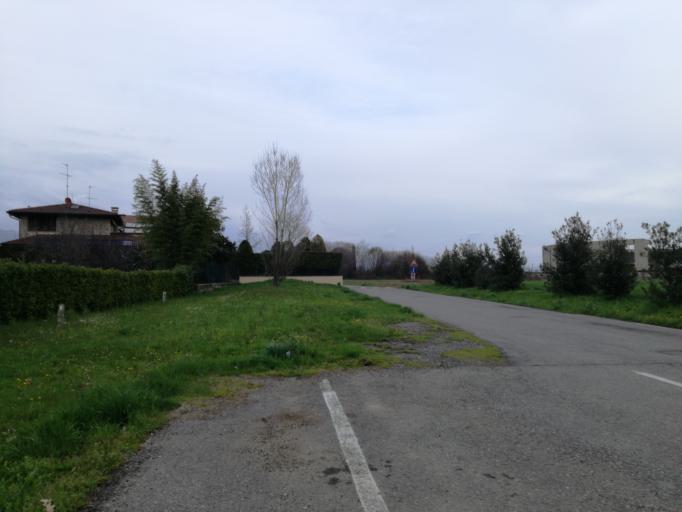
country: IT
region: Lombardy
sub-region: Provincia di Lecco
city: Verderio Superiore
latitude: 45.6664
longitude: 9.4439
